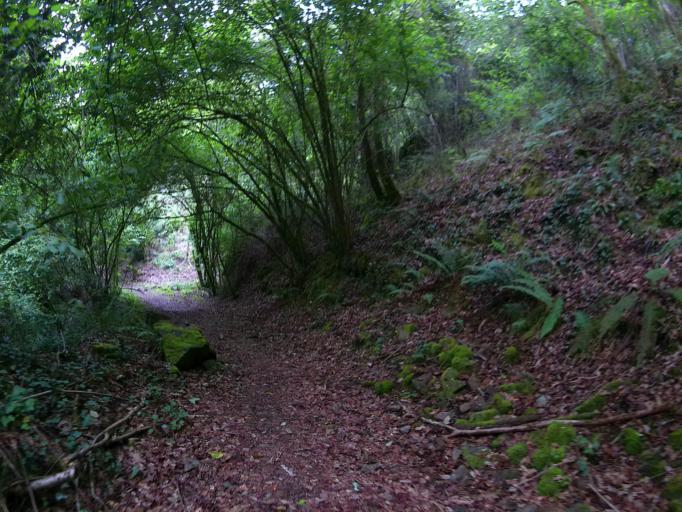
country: PT
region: Aveiro
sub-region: Albergaria-A-Velha
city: Branca
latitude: 40.7439
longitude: -8.4324
